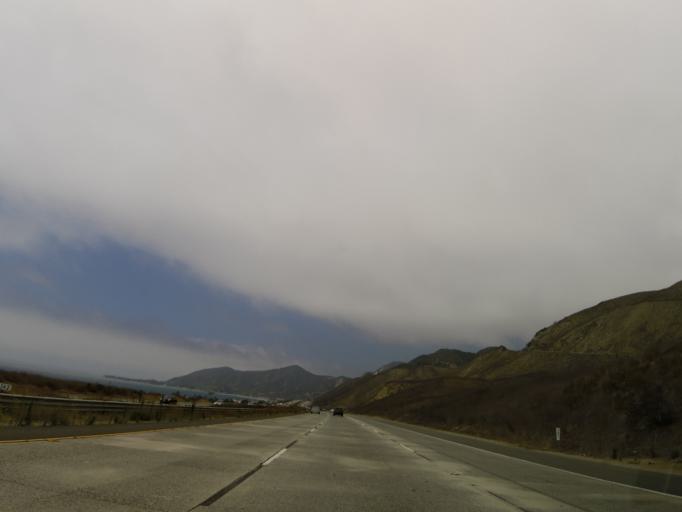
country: US
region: California
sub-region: Ventura County
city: Ventura
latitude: 34.3072
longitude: -119.3497
